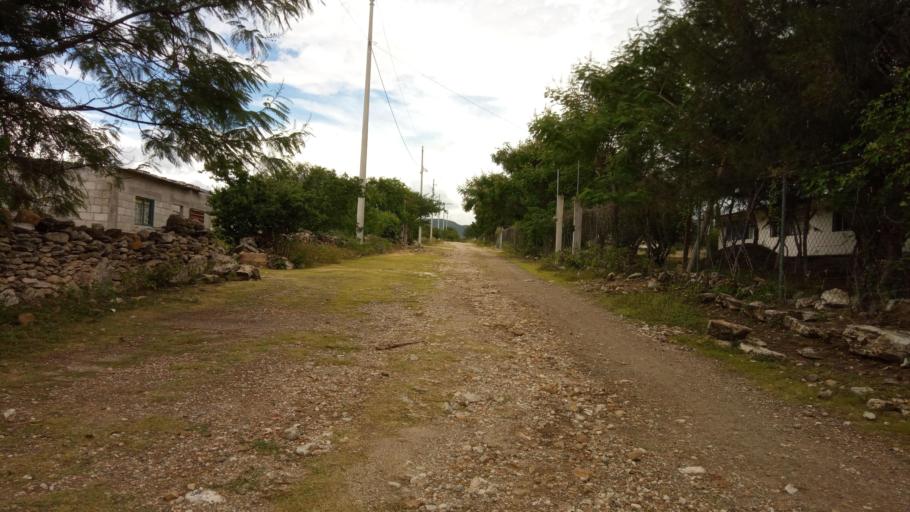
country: MX
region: Puebla
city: Totoltepec de Guerrero
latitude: 18.2957
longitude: -97.7744
